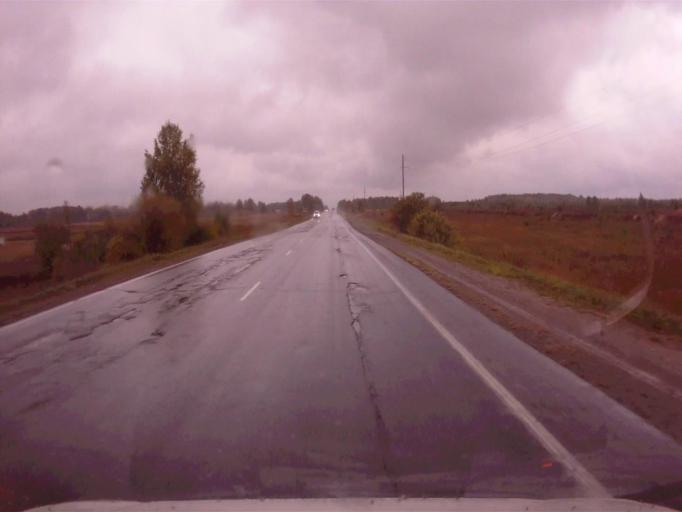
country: RU
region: Chelyabinsk
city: Novogornyy
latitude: 55.4882
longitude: 60.7064
